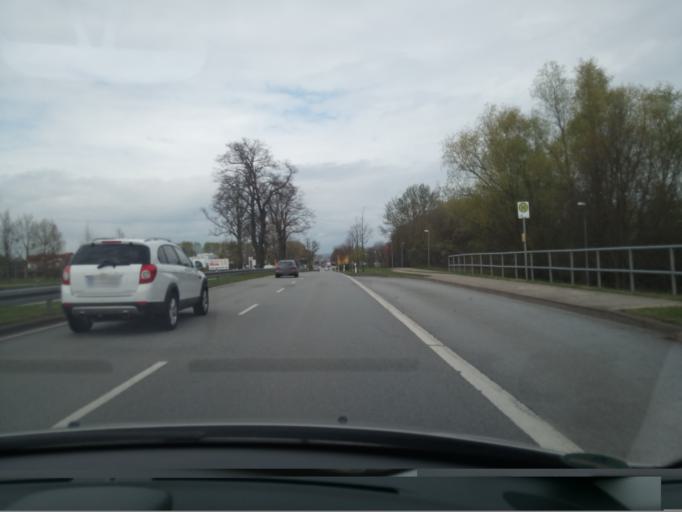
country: DE
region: Mecklenburg-Vorpommern
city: Neubrandenburg
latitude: 53.5217
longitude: 13.2611
